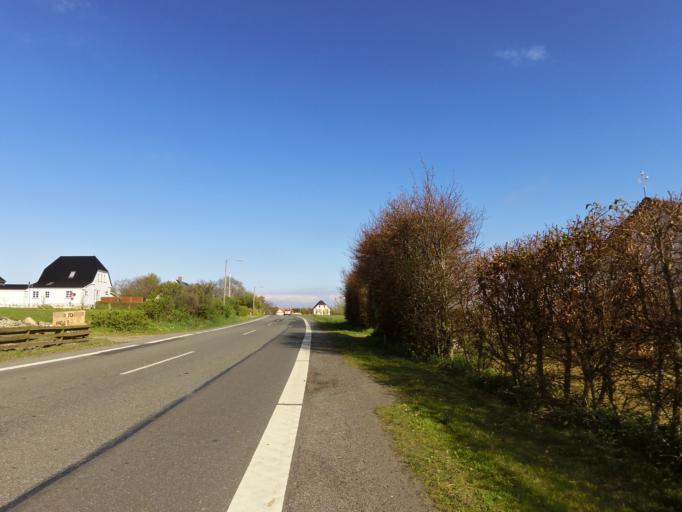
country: DK
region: South Denmark
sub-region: Tonder Kommune
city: Sherrebek
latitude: 55.1563
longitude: 8.8224
